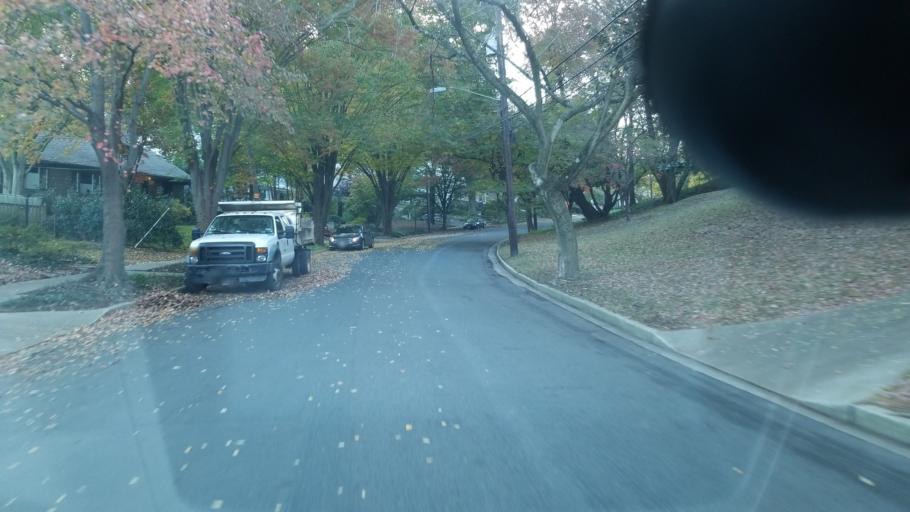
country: US
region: Maryland
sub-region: Montgomery County
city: Chevy Chase
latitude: 38.9569
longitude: -77.0638
